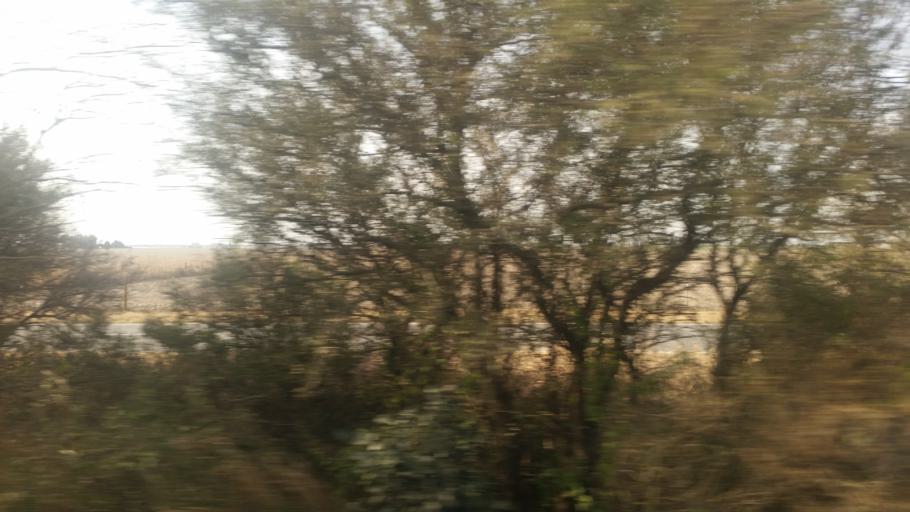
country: AR
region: Cordoba
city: Laguna Larga
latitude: -31.7554
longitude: -63.8218
